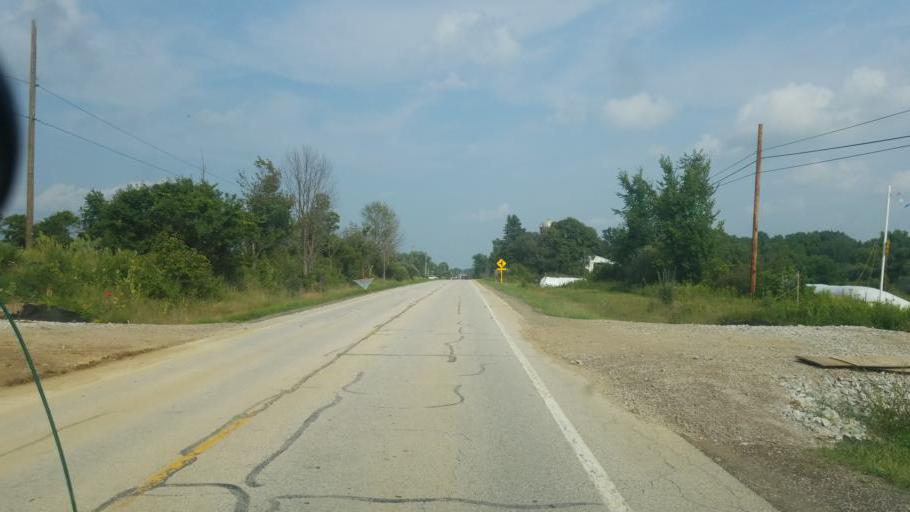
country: US
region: Ohio
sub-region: Medina County
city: Medina
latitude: 41.1674
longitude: -81.9624
